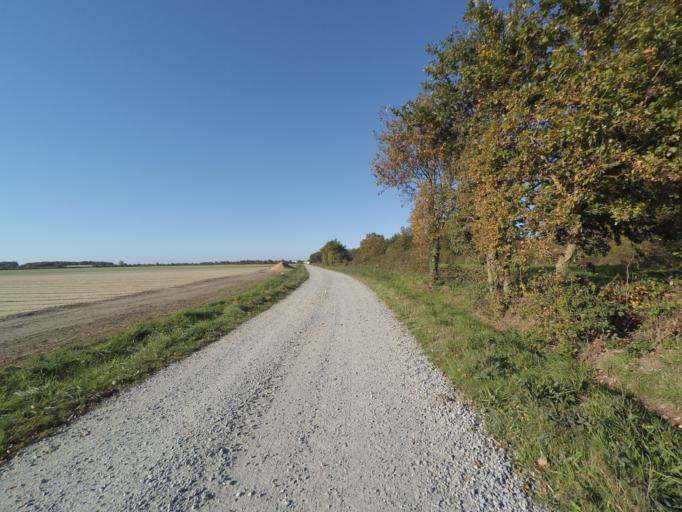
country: FR
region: Pays de la Loire
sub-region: Departement de la Loire-Atlantique
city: Remouille
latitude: 47.0089
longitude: -1.3812
